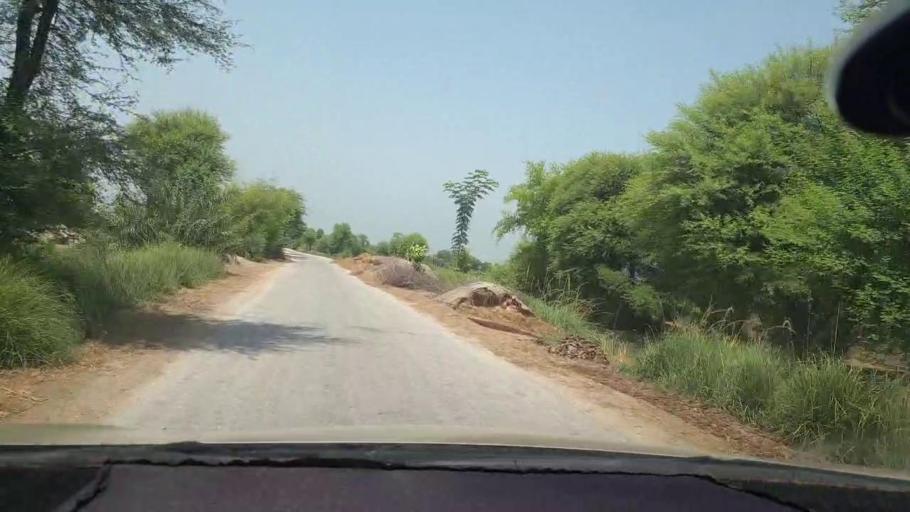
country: PK
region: Sindh
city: Kambar
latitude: 27.6512
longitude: 67.9658
